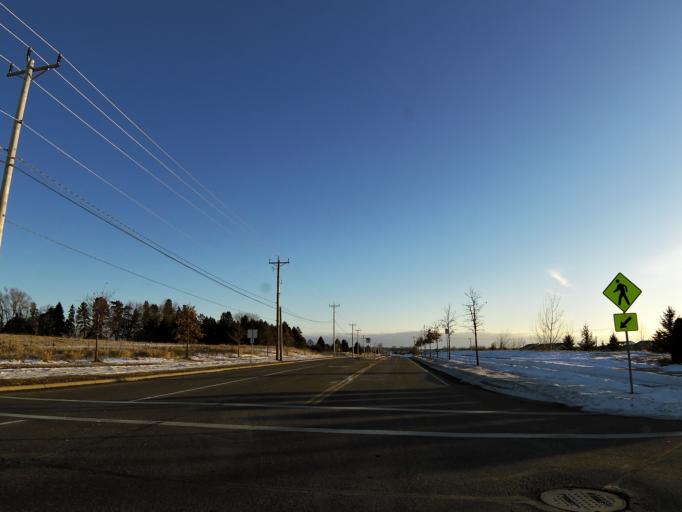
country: US
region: Minnesota
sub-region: Washington County
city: Woodbury
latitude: 44.8933
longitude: -92.8830
